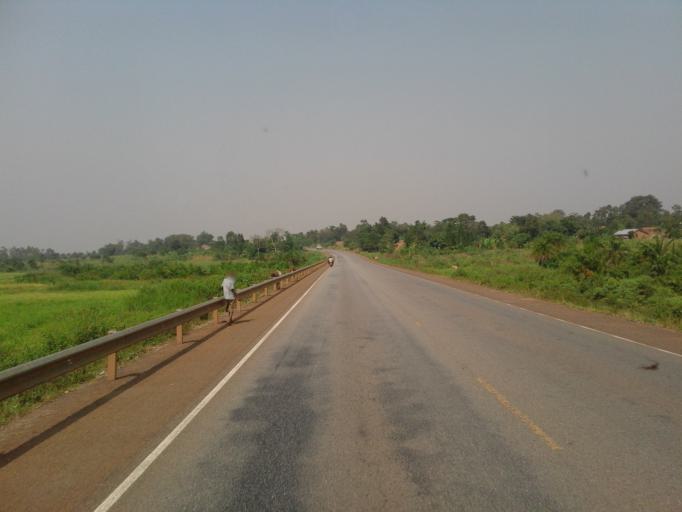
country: UG
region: Eastern Region
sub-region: Iganga District
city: Iganga
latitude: 0.6314
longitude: 33.5485
